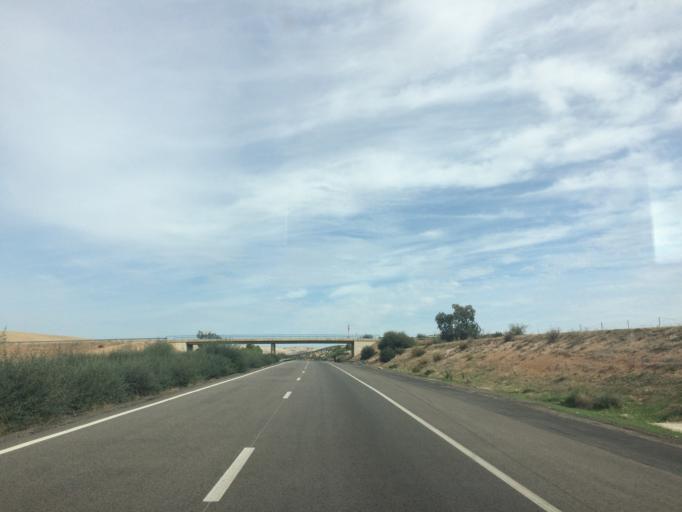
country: MA
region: Rabat-Sale-Zemmour-Zaer
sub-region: Khemisset
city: Khemisset
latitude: 33.8092
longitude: -5.8635
